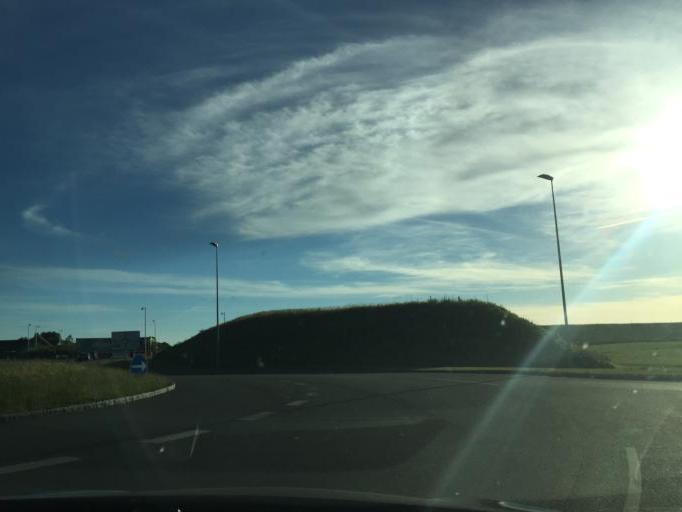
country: DK
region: Zealand
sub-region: Slagelse Kommune
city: Slagelse
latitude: 55.3883
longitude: 11.3224
